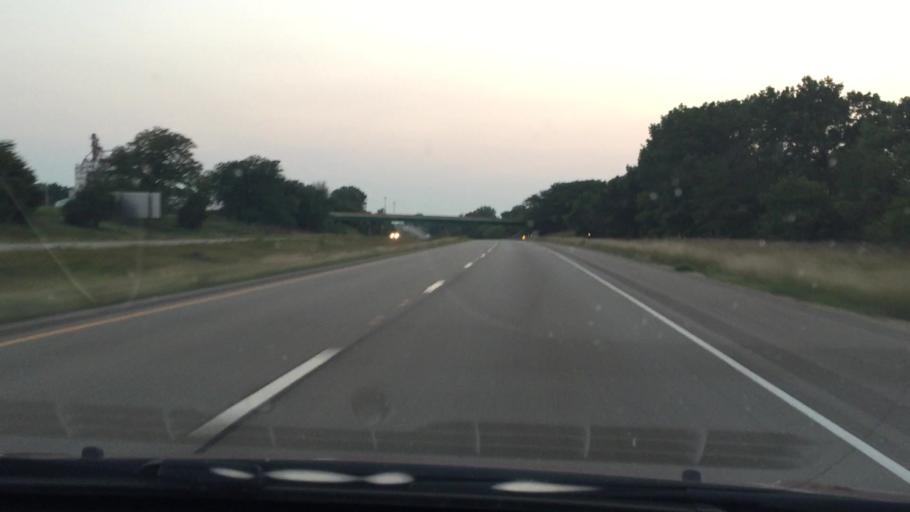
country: US
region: Illinois
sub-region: Bureau County
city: Princeton
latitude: 41.3956
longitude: -89.5001
